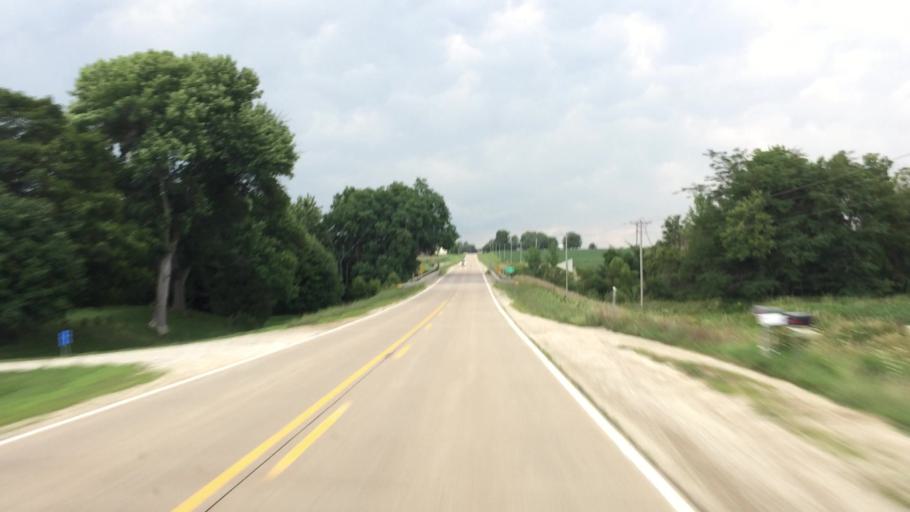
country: US
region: Iowa
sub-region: Lee County
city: Fort Madison
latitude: 40.7227
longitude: -91.3298
